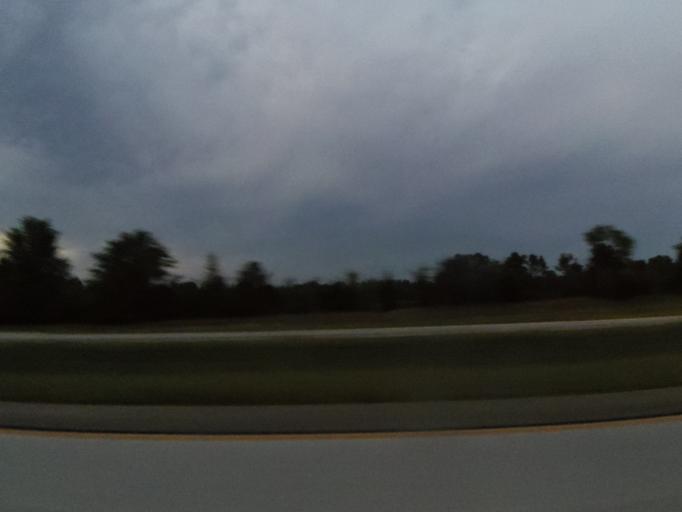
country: US
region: Georgia
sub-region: McDuffie County
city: Thomson
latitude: 33.5115
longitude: -82.4506
